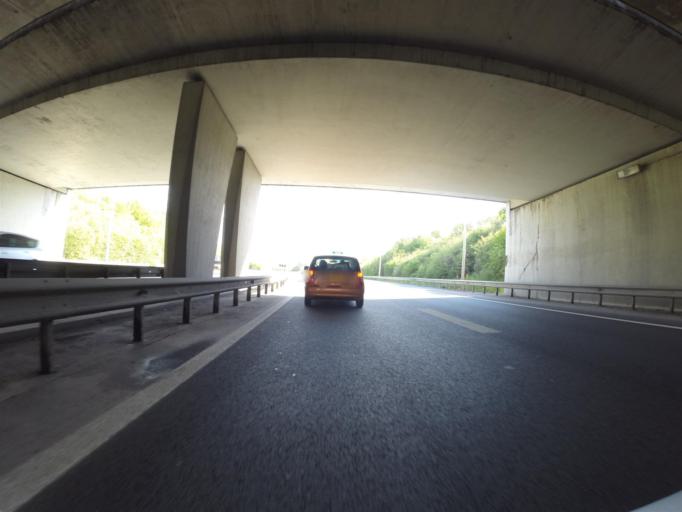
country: LU
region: Luxembourg
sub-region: Canton de Luxembourg
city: Hesperange
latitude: 49.5768
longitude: 6.1247
